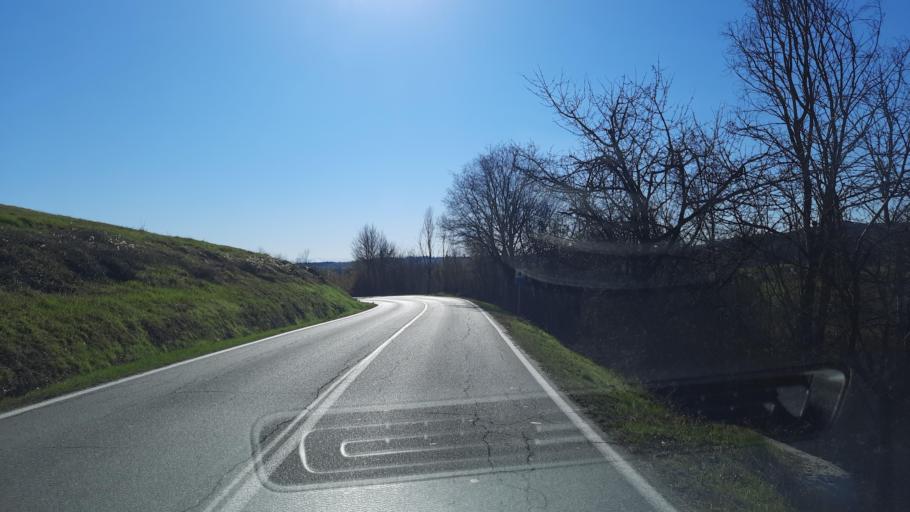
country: IT
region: Piedmont
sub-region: Provincia di Alessandria
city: Rosignano Monferrato
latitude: 45.0800
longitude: 8.4110
